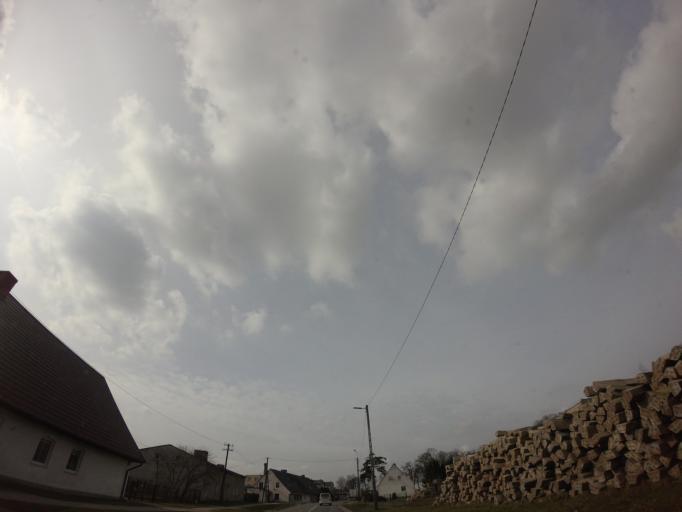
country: PL
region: West Pomeranian Voivodeship
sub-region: Powiat walecki
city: Walcz
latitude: 53.3150
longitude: 16.3436
